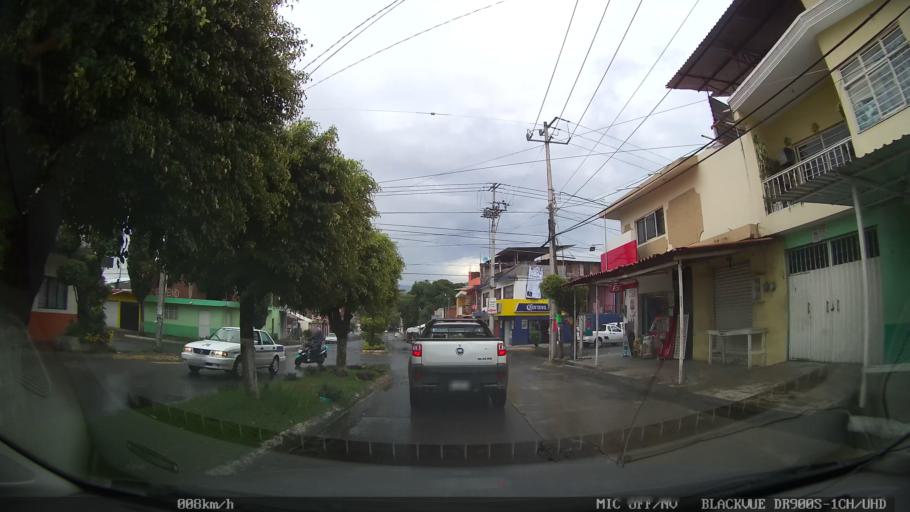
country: MX
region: Michoacan
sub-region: Uruapan
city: Santa Rosa (Santa Barbara)
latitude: 19.3888
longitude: -102.0538
